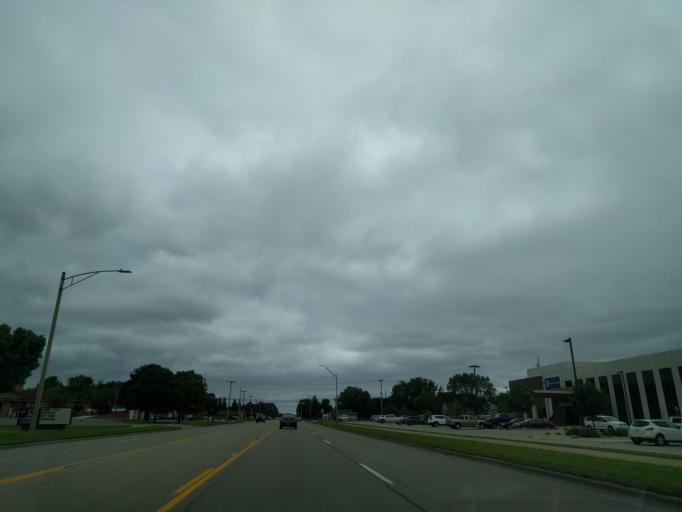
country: US
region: Michigan
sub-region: Delta County
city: Escanaba
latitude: 45.7370
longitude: -87.0799
